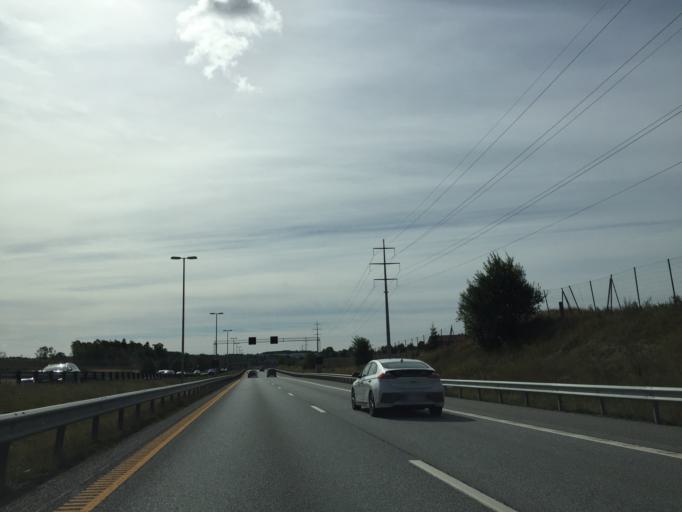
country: NO
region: Akershus
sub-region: Vestby
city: Vestby
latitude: 59.6094
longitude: 10.7338
